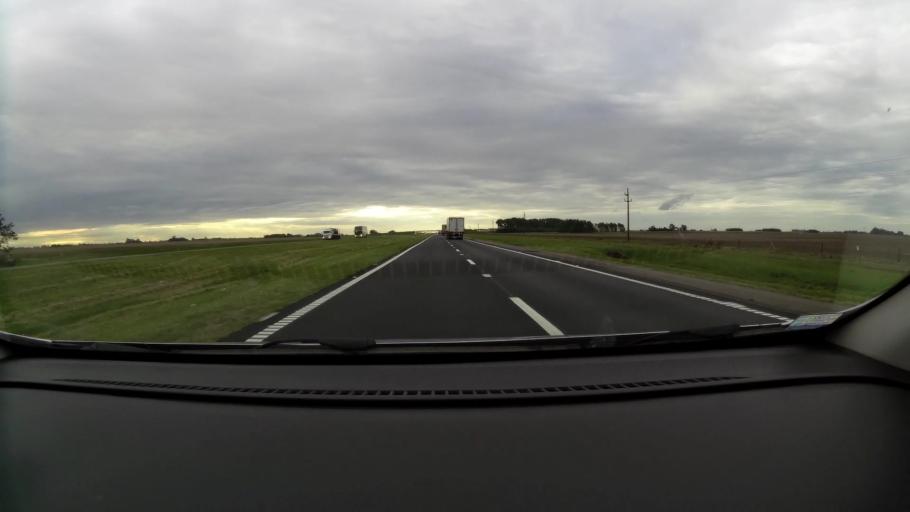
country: AR
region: Buenos Aires
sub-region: Partido de Ramallo
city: Ramallo
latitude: -33.6125
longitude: -60.0161
